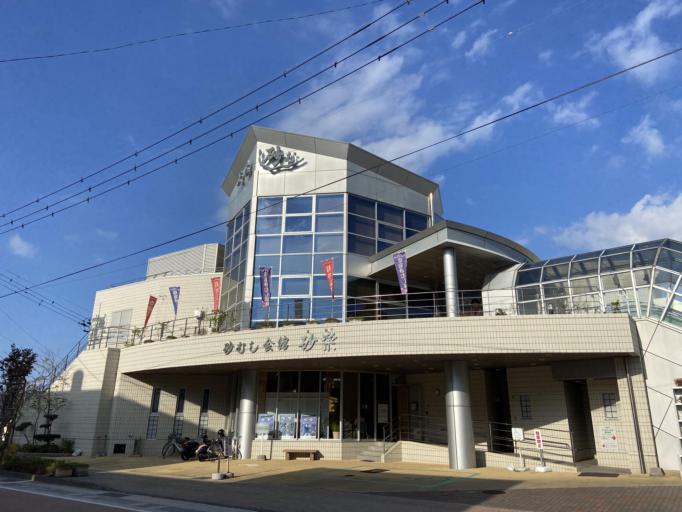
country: JP
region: Kagoshima
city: Ibusuki
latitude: 31.2297
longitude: 130.6517
